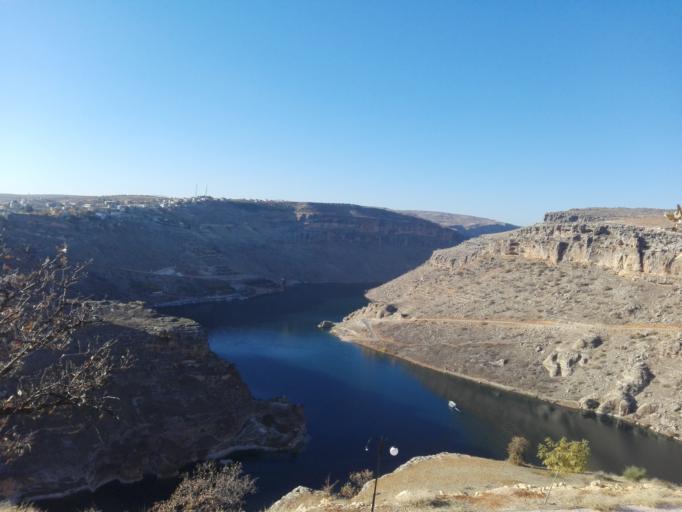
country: TR
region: Diyarbakir
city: Egil
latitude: 38.2555
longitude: 40.1004
